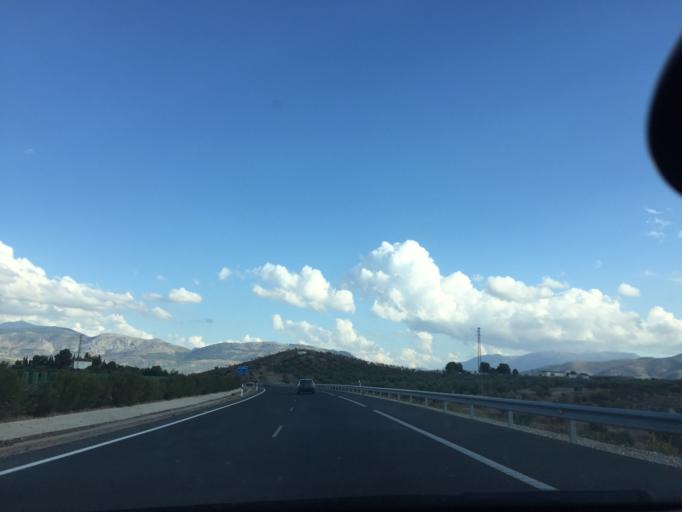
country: ES
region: Andalusia
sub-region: Provincia de Jaen
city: Jaen
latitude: 37.8054
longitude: -3.7322
